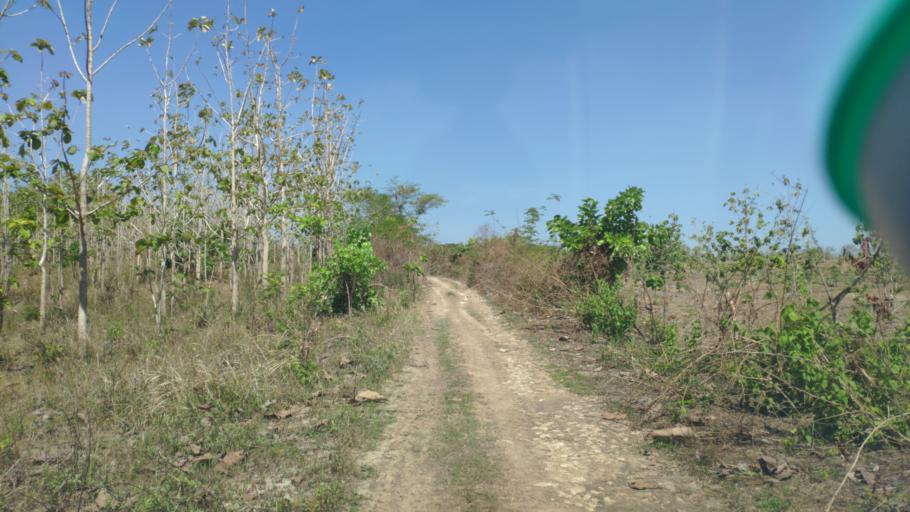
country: ID
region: Central Java
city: Suruhan
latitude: -7.0086
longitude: 111.5554
